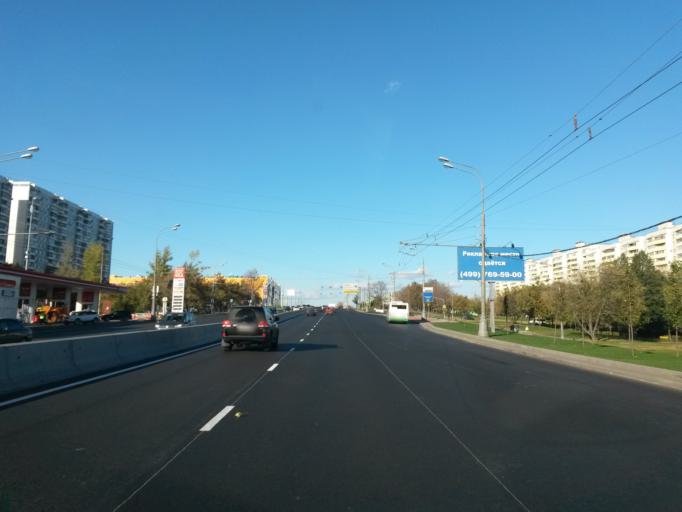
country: RU
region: Moscow
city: Chertanovo Yuzhnoye
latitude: 55.6055
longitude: 37.6069
